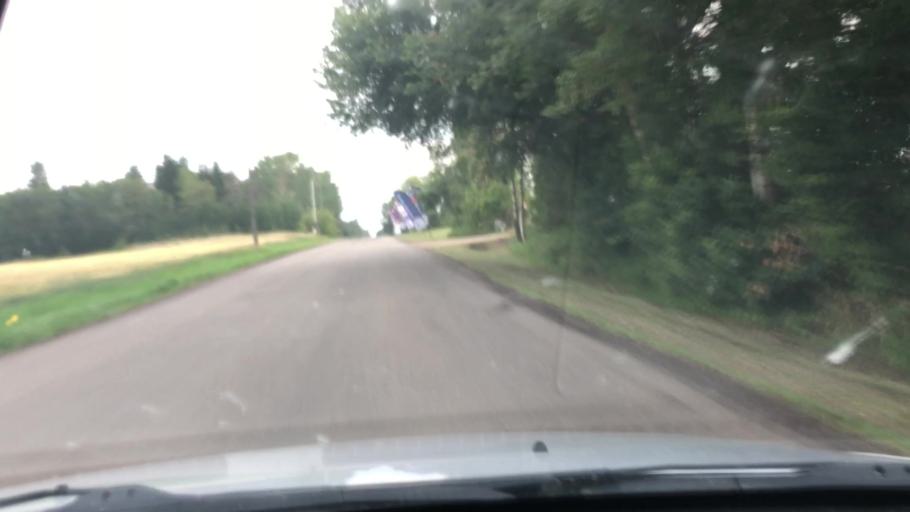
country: CA
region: Alberta
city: Devon
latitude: 53.4191
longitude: -113.6892
